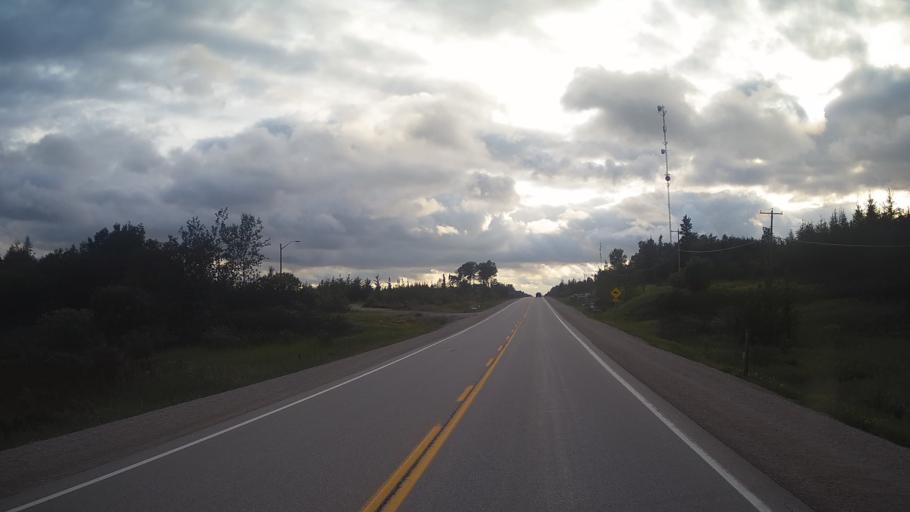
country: CA
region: Ontario
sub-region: Rainy River District
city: Atikokan
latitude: 49.0509
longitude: -90.4845
